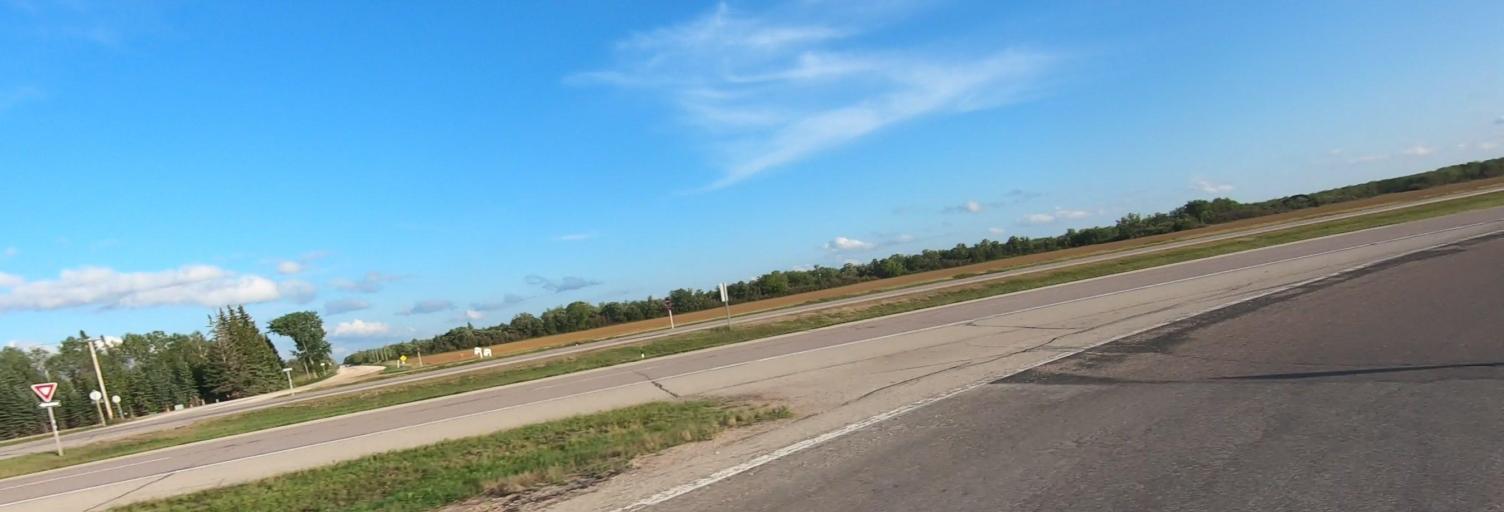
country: CA
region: Manitoba
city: Selkirk
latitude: 50.1142
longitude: -96.8421
